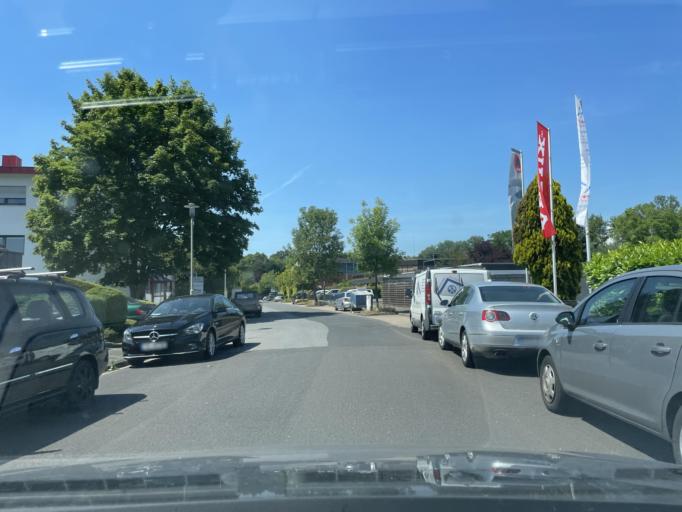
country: DE
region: North Rhine-Westphalia
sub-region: Regierungsbezirk Dusseldorf
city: Monchengladbach
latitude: 51.2290
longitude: 6.4715
